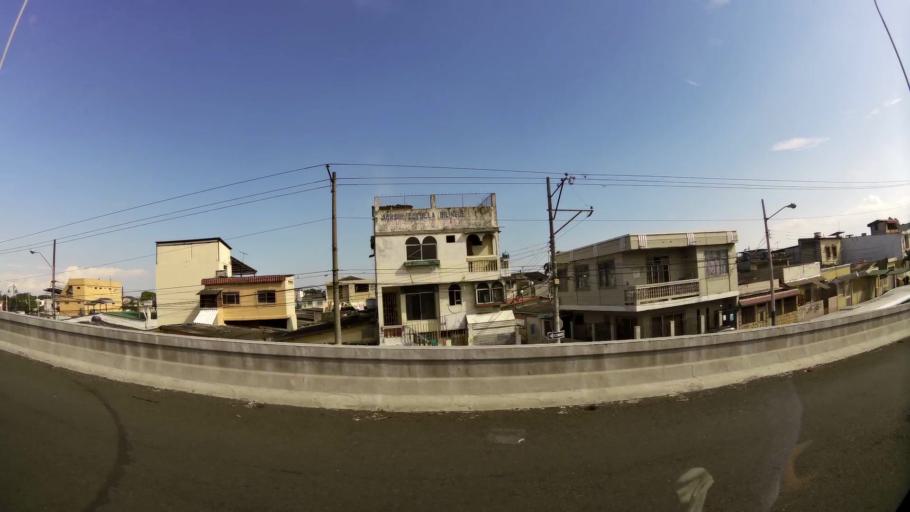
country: EC
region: Guayas
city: Guayaquil
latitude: -2.2217
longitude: -79.9024
